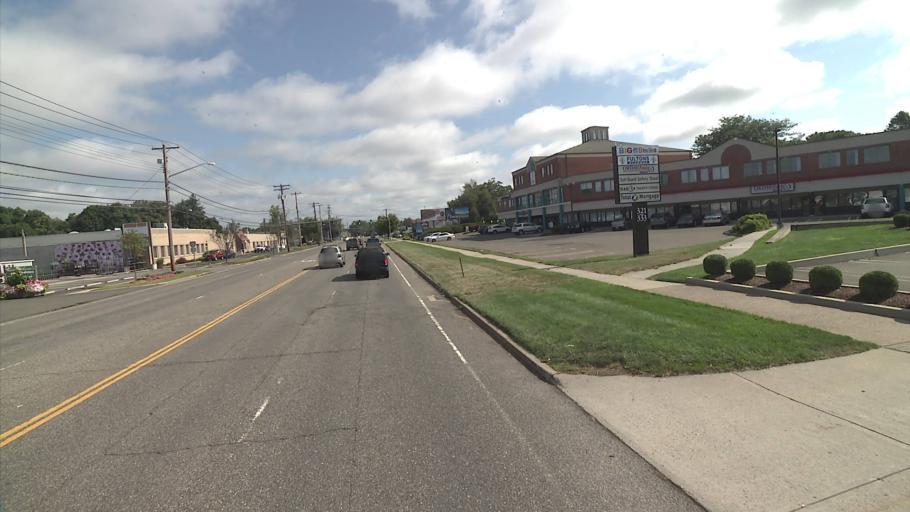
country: US
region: Connecticut
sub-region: New Haven County
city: City of Milford (balance)
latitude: 41.2236
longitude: -73.0722
